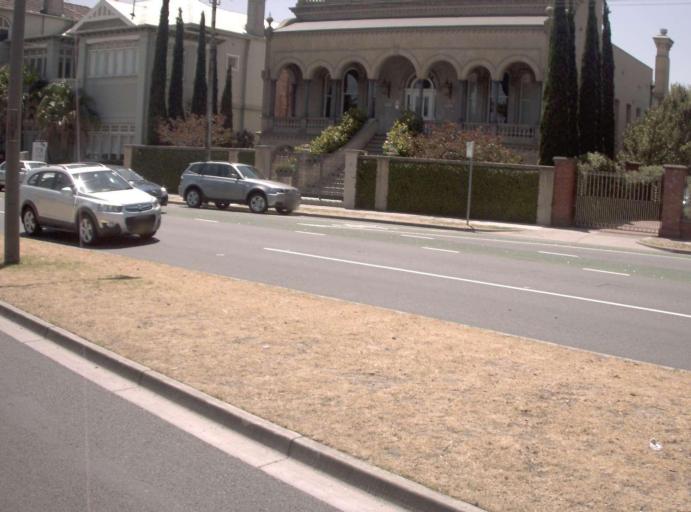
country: AU
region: Victoria
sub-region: Port Phillip
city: St Kilda West
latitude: -37.8611
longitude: 144.9725
